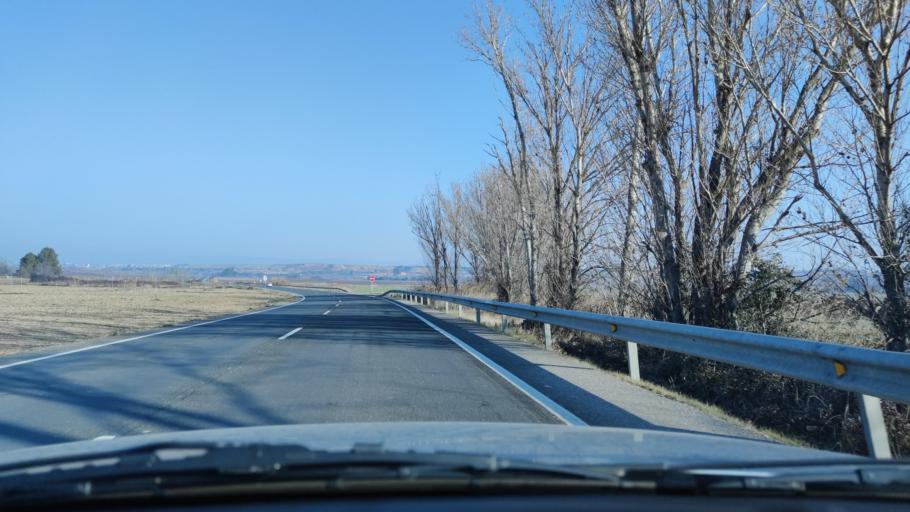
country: ES
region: Catalonia
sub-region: Provincia de Lleida
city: Albesa
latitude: 41.7108
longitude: 0.6388
